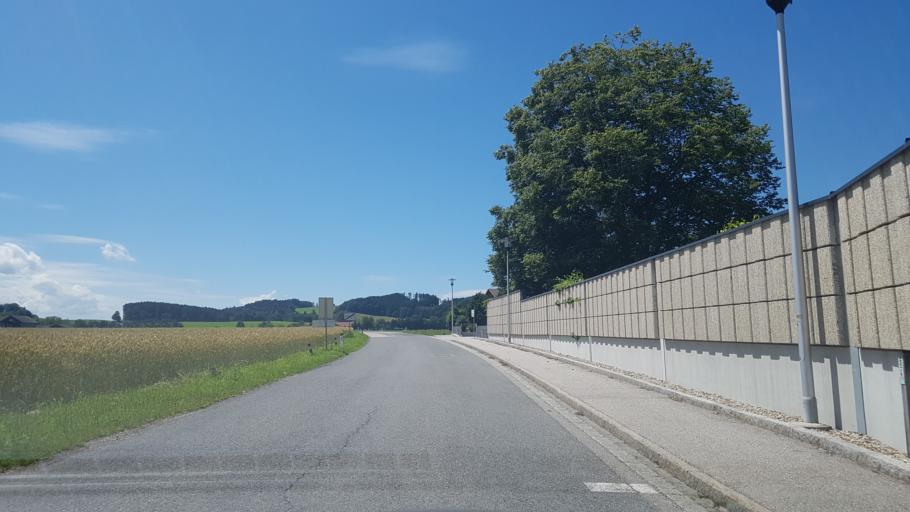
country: AT
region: Salzburg
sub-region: Politischer Bezirk Salzburg-Umgebung
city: Schleedorf
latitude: 48.0071
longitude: 13.1750
